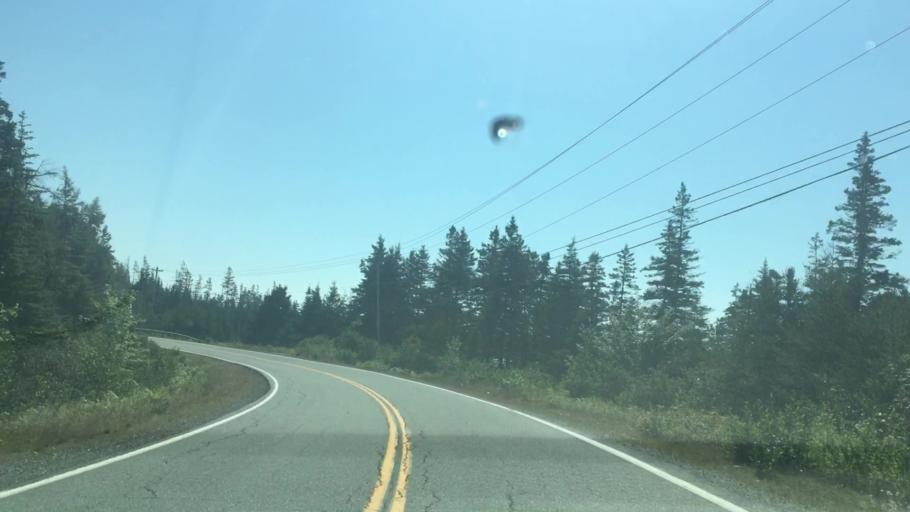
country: CA
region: Nova Scotia
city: Antigonish
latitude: 45.0080
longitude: -62.0900
